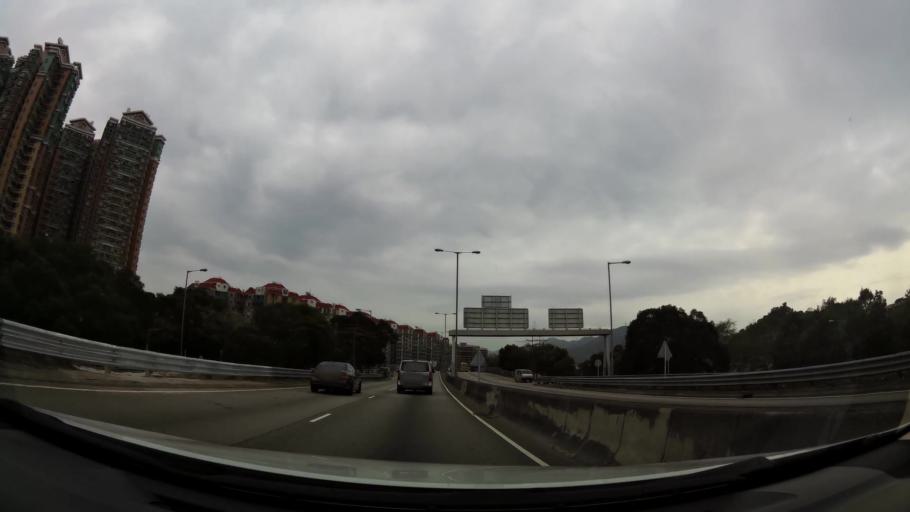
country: HK
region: Yuen Long
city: Yuen Long Kau Hui
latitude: 22.4452
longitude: 114.0167
